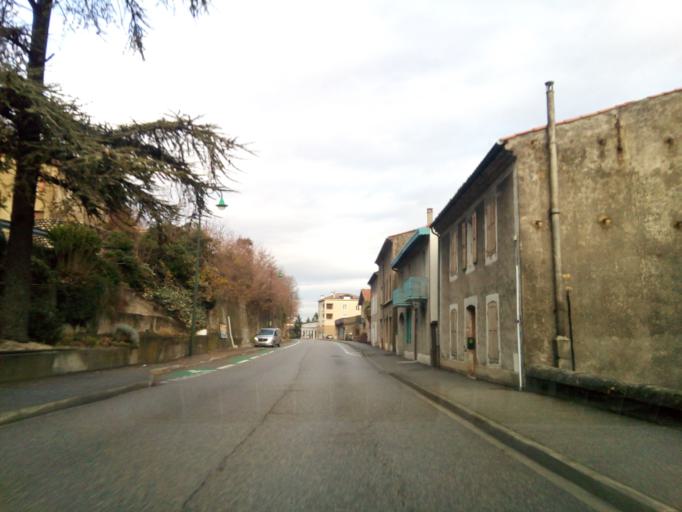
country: FR
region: Rhone-Alpes
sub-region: Departement de l'Ardeche
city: Beauchastel
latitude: 44.8267
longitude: 4.8035
